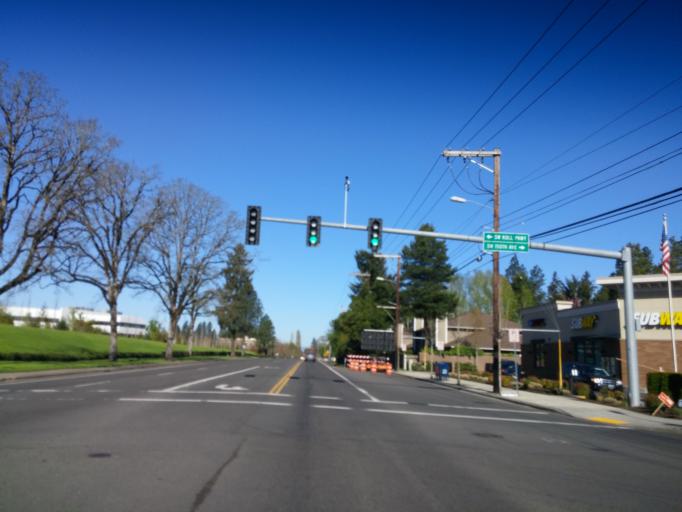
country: US
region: Oregon
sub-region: Washington County
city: Cedar Mill
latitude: 45.5147
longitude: -122.8322
